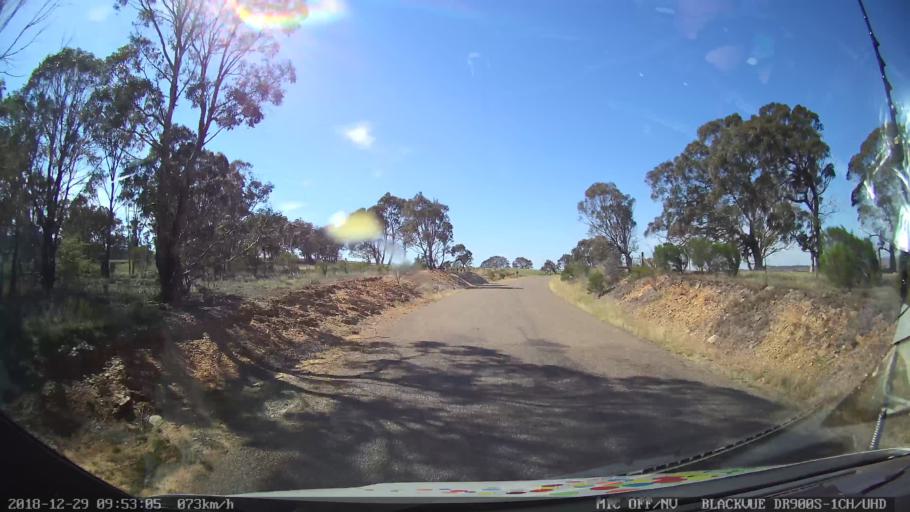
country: AU
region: New South Wales
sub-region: Goulburn Mulwaree
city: Goulburn
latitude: -34.7478
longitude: 149.4697
